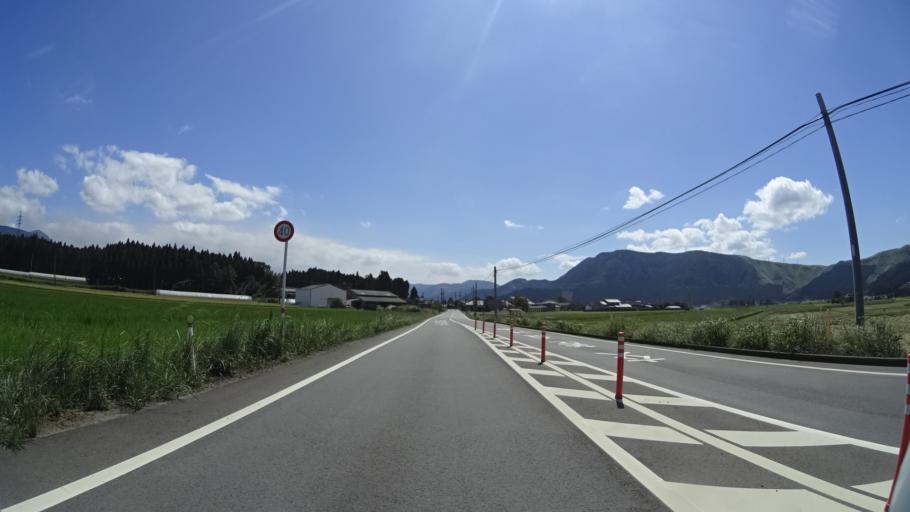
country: JP
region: Kumamoto
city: Aso
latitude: 32.9229
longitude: 130.9942
